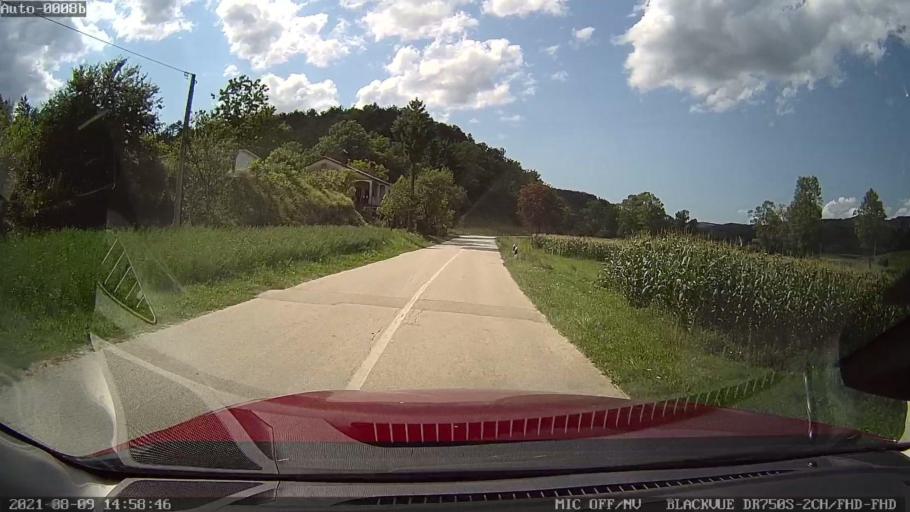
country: HR
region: Istarska
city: Pazin
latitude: 45.2653
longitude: 14.0369
